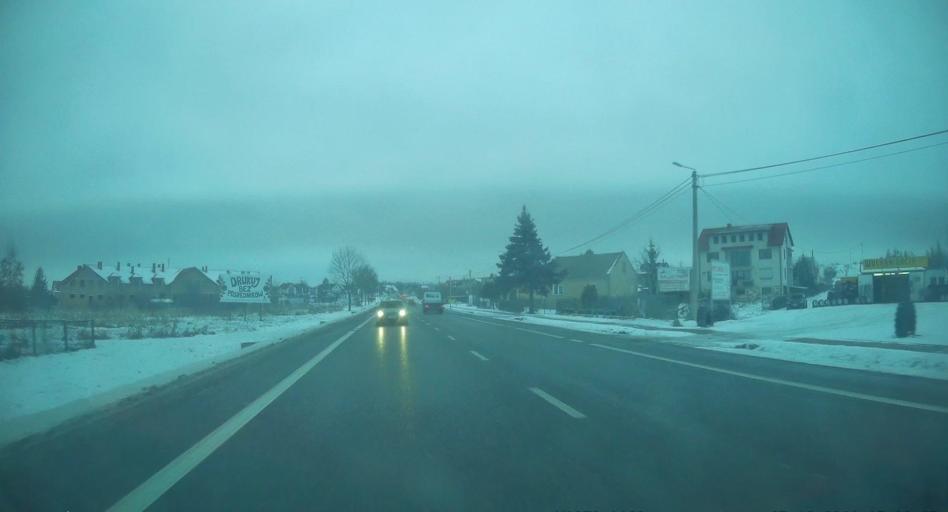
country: PL
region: Swietokrzyskie
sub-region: Powiat kielecki
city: Kostomloty Drugie
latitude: 50.9223
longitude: 20.5680
